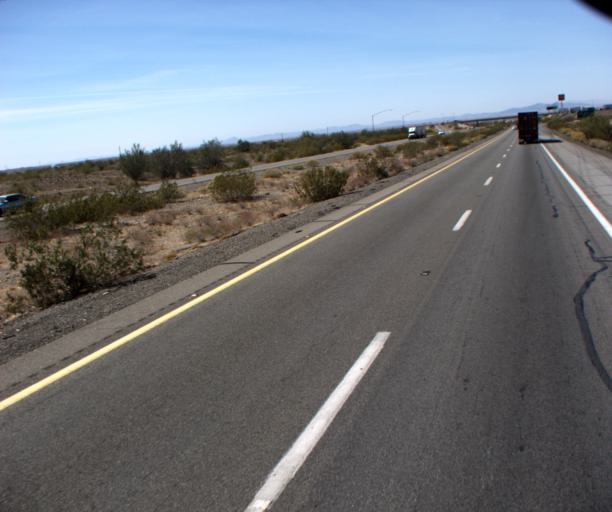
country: US
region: Arizona
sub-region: La Paz County
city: Ehrenberg
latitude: 33.6262
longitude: -114.4281
